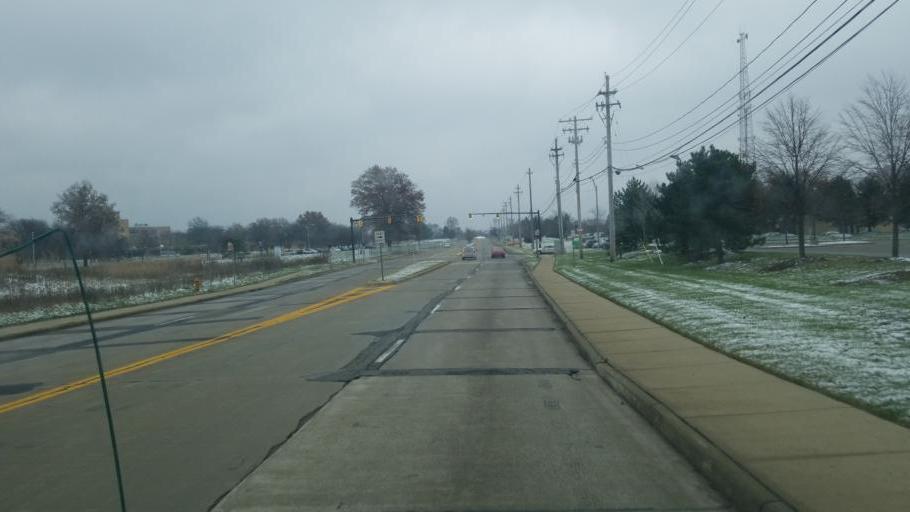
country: US
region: Ohio
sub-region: Cuyahoga County
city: Brecksville
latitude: 41.2893
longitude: -81.6344
